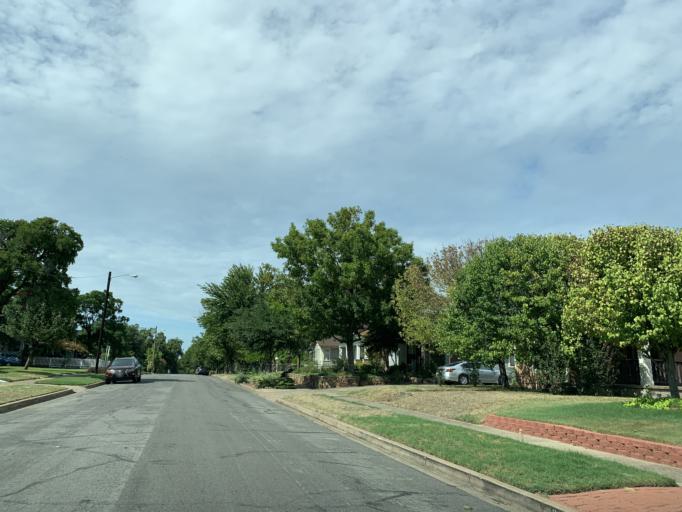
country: US
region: Texas
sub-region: Dallas County
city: Cockrell Hill
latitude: 32.7395
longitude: -96.8503
